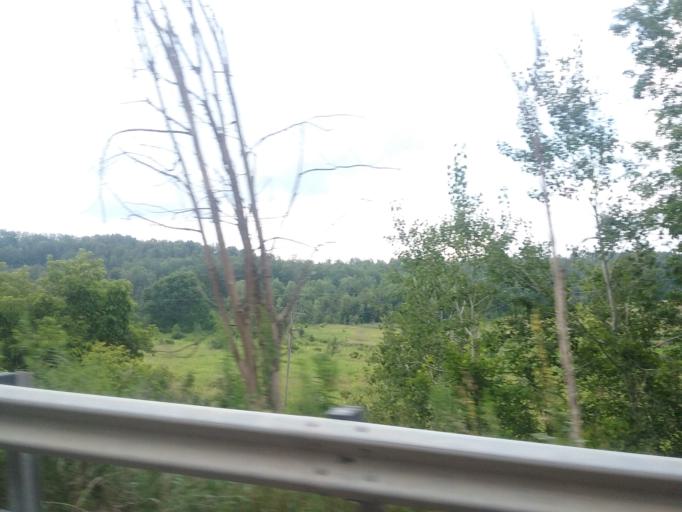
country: US
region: Pennsylvania
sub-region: Tioga County
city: Wellsboro
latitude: 41.7526
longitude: -77.2367
